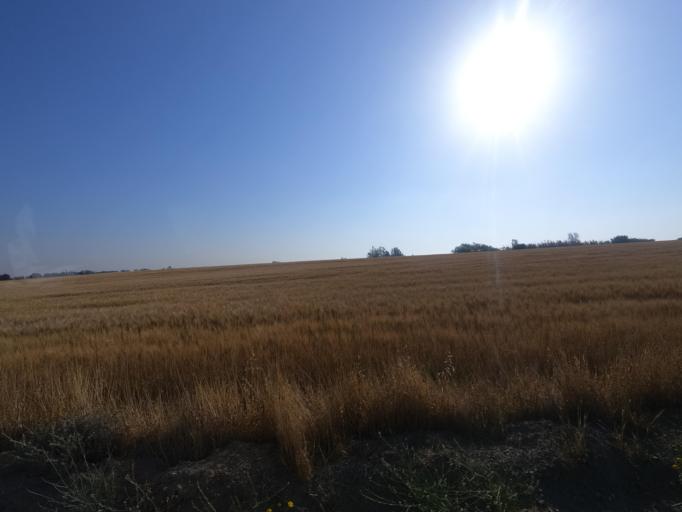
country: CY
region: Ammochostos
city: Acheritou
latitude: 35.0883
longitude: 33.9039
